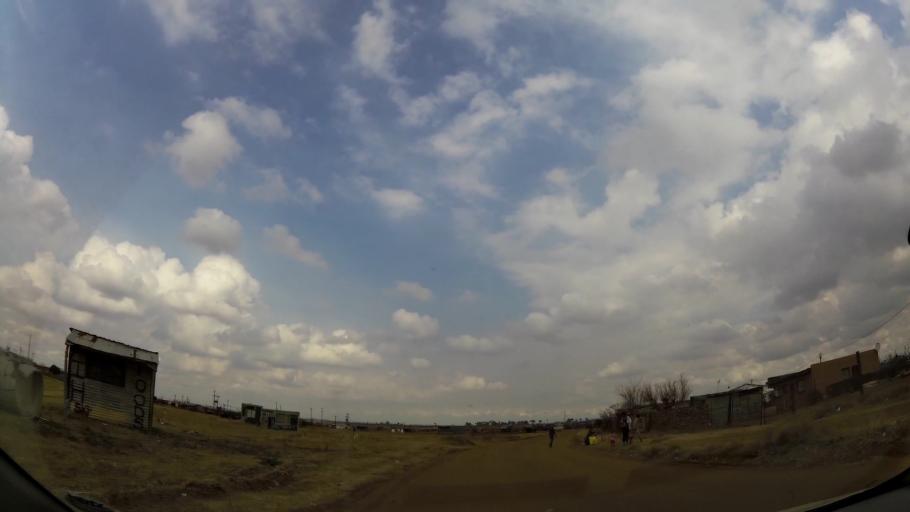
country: ZA
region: Orange Free State
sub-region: Fezile Dabi District Municipality
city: Sasolburg
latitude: -26.8596
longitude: 27.8949
